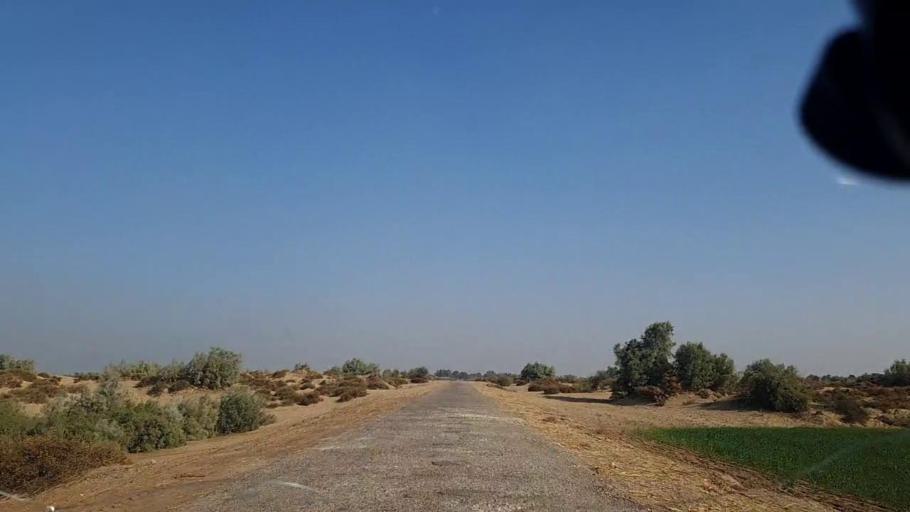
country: PK
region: Sindh
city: Khanpur
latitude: 27.6867
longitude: 69.4739
